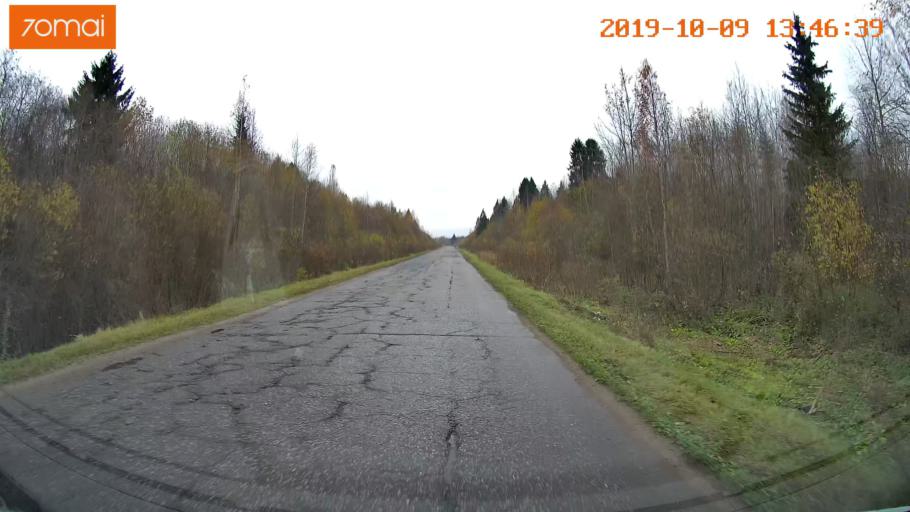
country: RU
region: Kostroma
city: Buy
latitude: 58.3852
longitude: 41.2192
